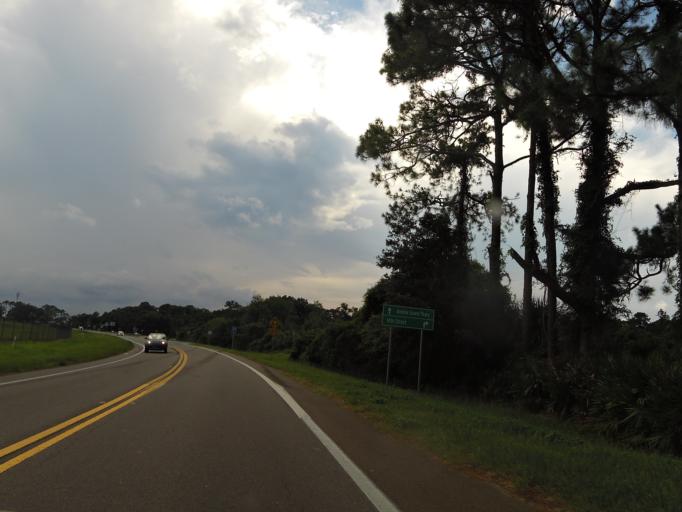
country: US
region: Florida
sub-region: Nassau County
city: Fernandina Beach
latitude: 30.6186
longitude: -81.4530
